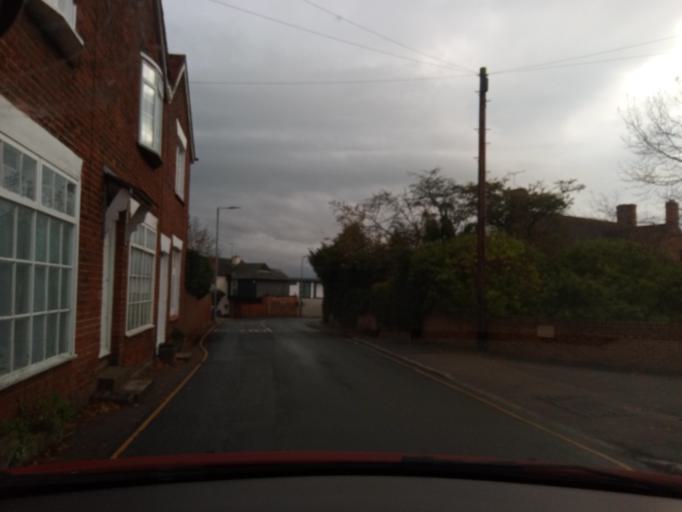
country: GB
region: England
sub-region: Essex
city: West Mersea
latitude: 51.7752
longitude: 0.9103
